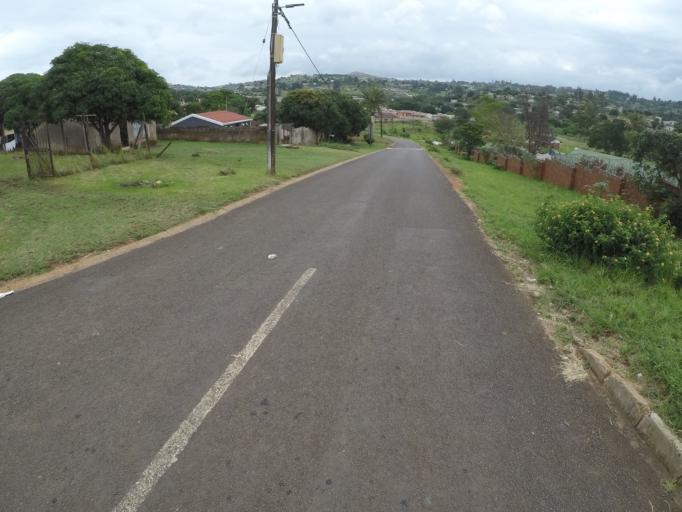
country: ZA
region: KwaZulu-Natal
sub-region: uThungulu District Municipality
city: Empangeni
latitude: -28.7681
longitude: 31.8689
